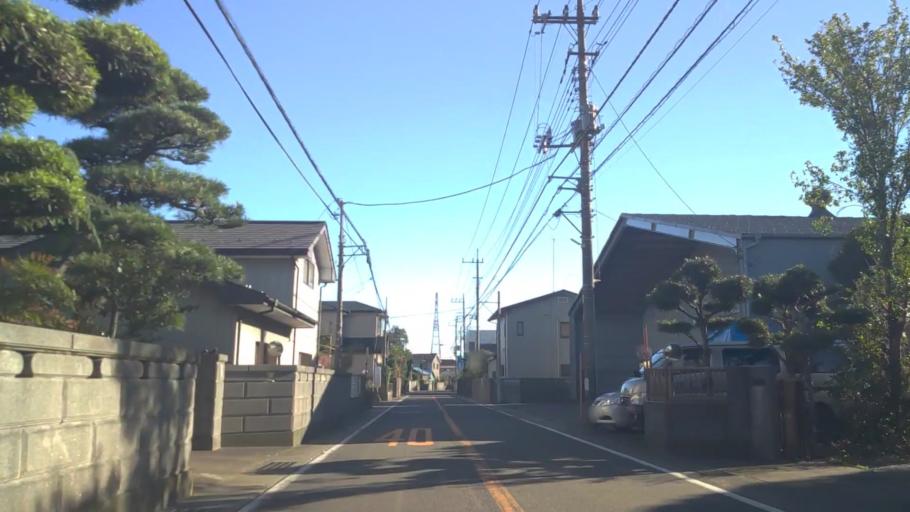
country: JP
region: Kanagawa
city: Atsugi
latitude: 35.4159
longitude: 139.3655
